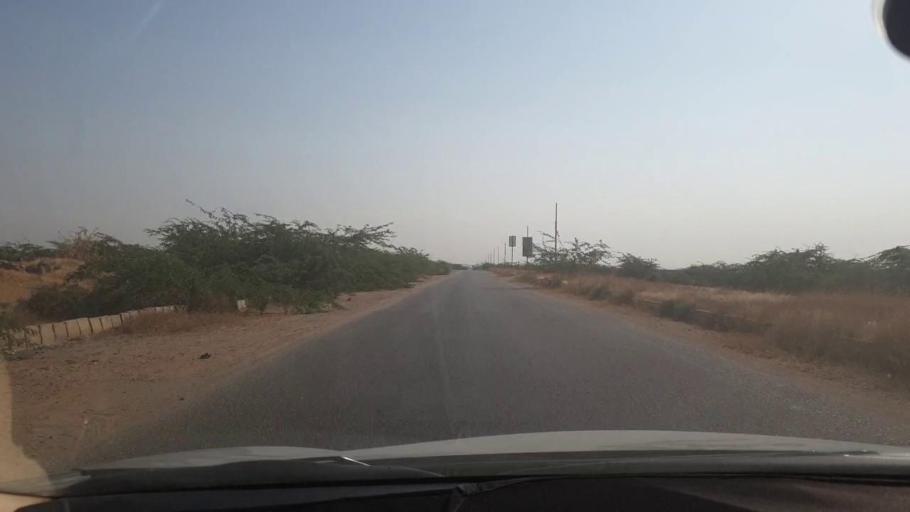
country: PK
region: Sindh
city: Malir Cantonment
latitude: 25.0691
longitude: 67.1388
